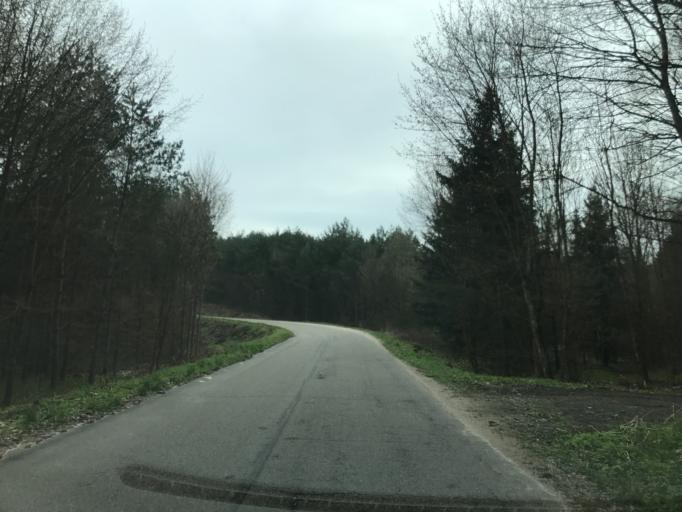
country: PL
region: Warmian-Masurian Voivodeship
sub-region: Powiat ostrodzki
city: Gierzwald
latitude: 53.6277
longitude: 20.1391
